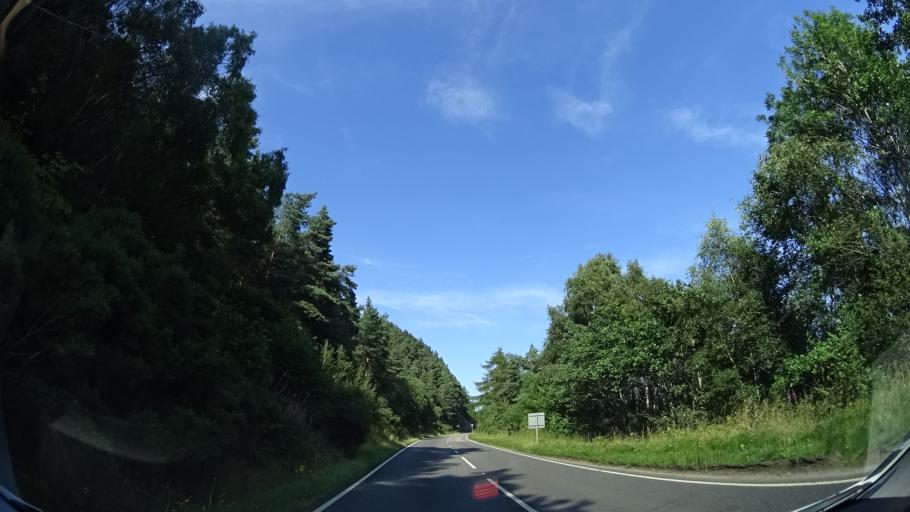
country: GB
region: Scotland
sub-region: Highland
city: Beauly
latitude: 57.3947
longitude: -4.3604
